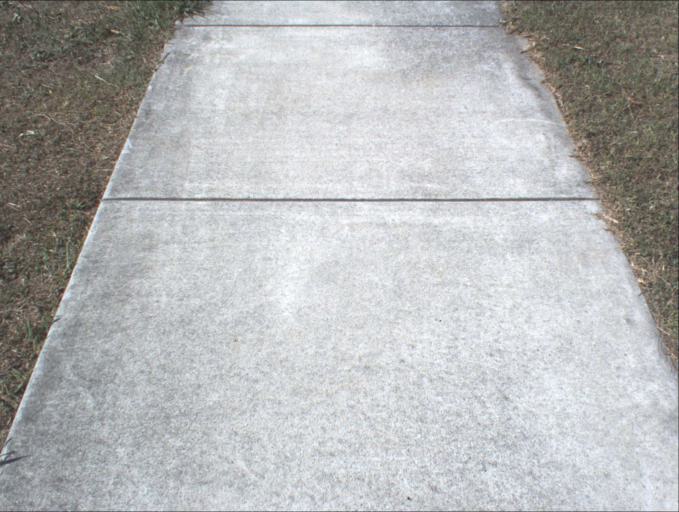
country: AU
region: Queensland
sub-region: Logan
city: Beenleigh
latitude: -27.6912
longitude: 153.2113
